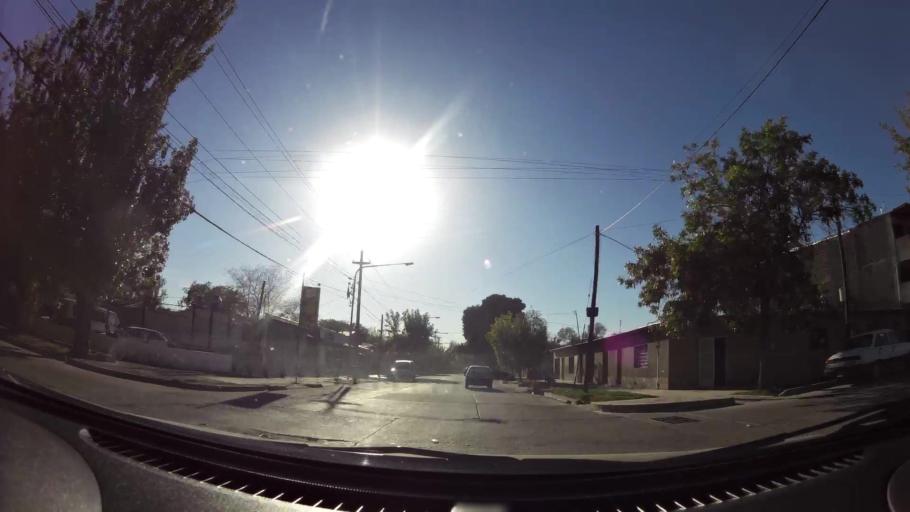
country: AR
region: Mendoza
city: Las Heras
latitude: -32.8539
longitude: -68.8324
